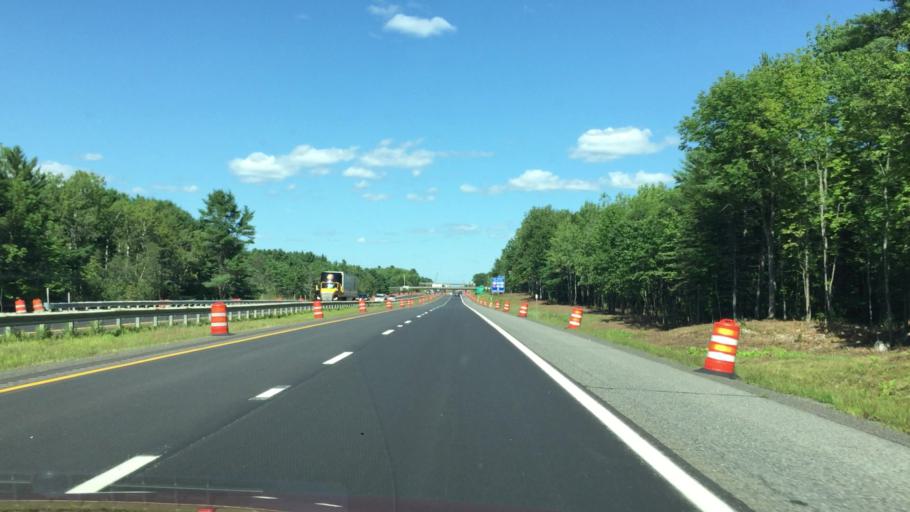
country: US
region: Maine
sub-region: Kennebec County
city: Gardiner
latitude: 44.2028
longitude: -69.8380
